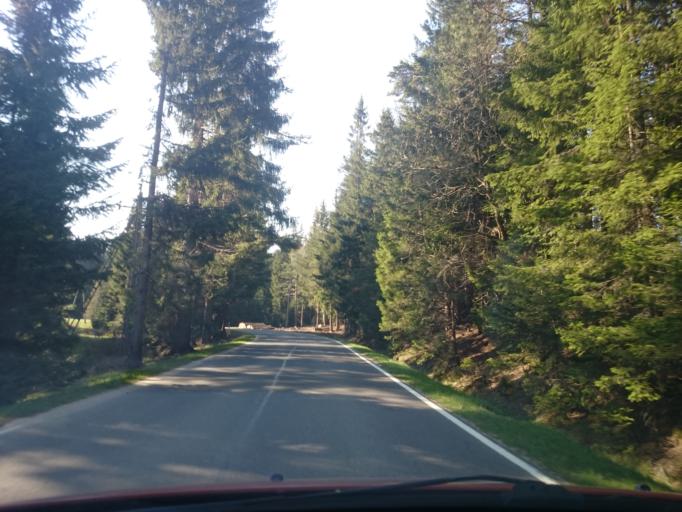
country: PL
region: Lower Silesian Voivodeship
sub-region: Powiat klodzki
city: Duszniki-Zdroj
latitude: 50.3246
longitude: 16.4318
